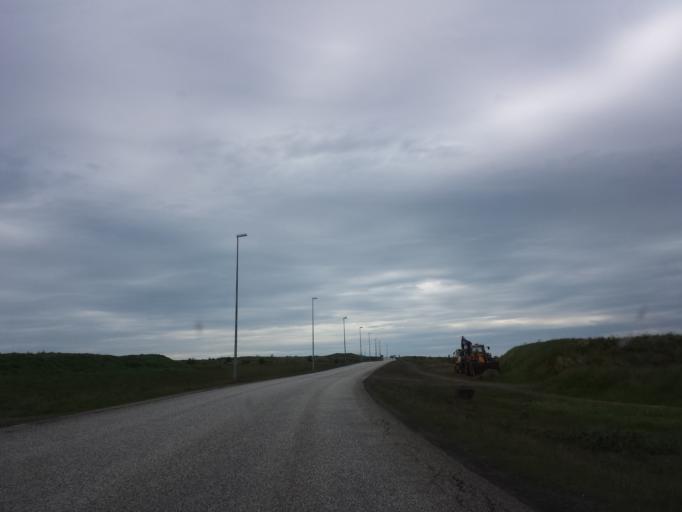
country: IS
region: Capital Region
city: Hafnarfjoerdur
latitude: 64.0865
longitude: -21.9747
